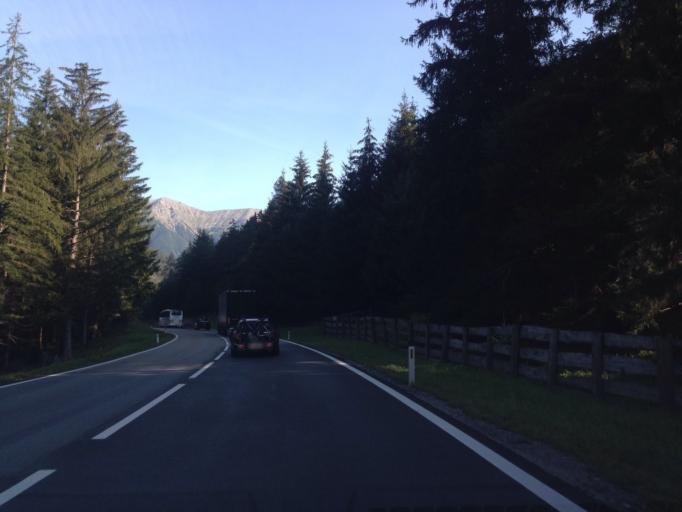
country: AT
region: Tyrol
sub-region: Politischer Bezirk Imst
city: Nassereith
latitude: 47.3311
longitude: 10.8186
